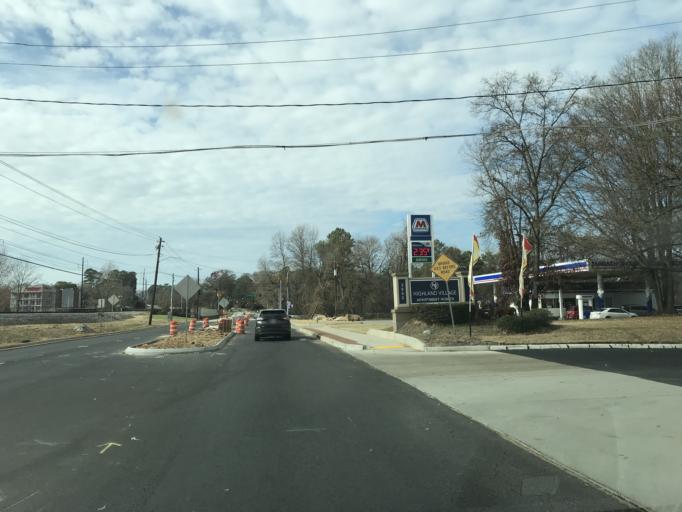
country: US
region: Georgia
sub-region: DeKalb County
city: Clarkston
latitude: 33.8036
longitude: -84.2482
